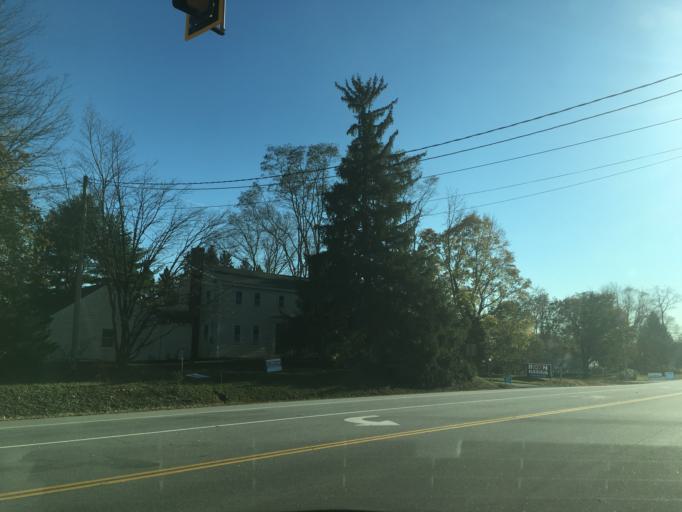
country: US
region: New Hampshire
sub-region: Rockingham County
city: Stratham Station
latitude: 43.0381
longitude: -70.9025
